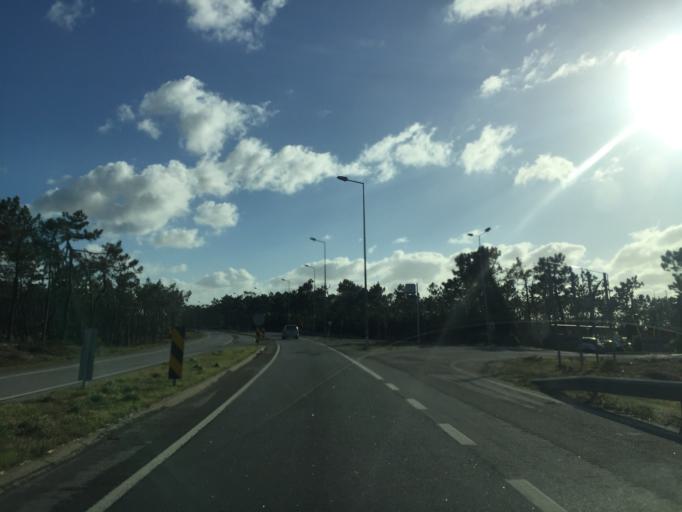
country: PT
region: Coimbra
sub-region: Figueira da Foz
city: Figueira da Foz
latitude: 40.1192
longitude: -8.8558
